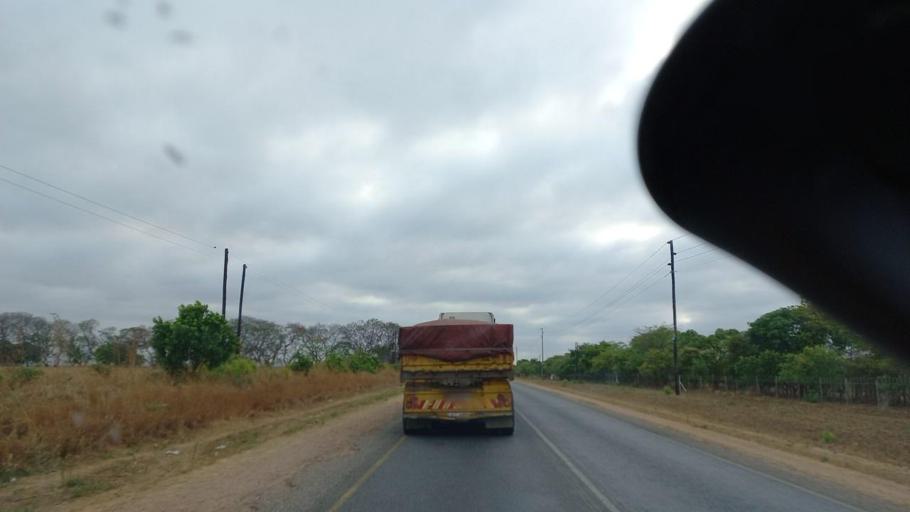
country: ZM
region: Lusaka
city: Chongwe
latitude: -15.3495
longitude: 28.5673
